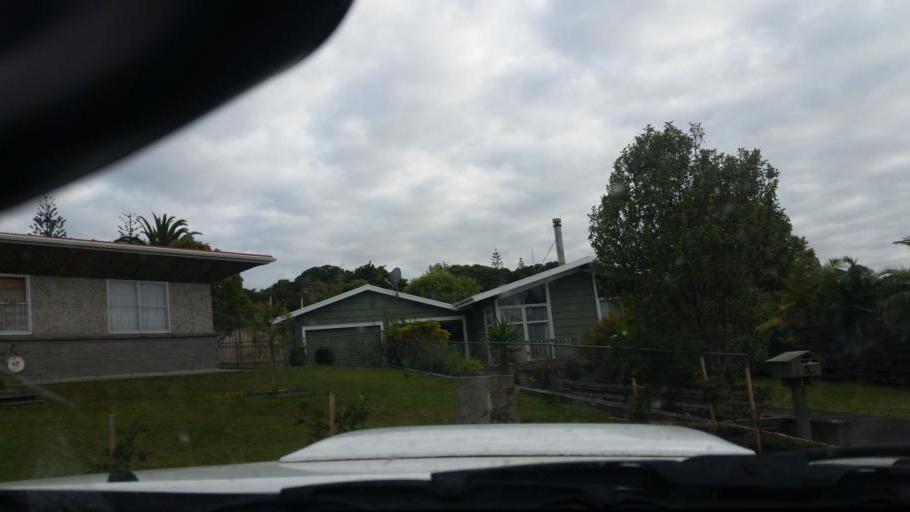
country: NZ
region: Northland
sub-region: Kaipara District
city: Dargaville
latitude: -35.9306
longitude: 173.8729
